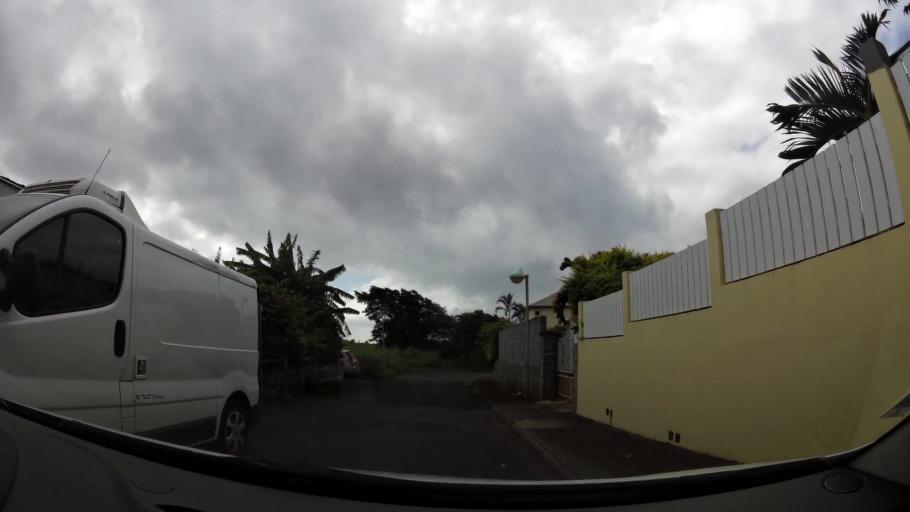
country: RE
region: Reunion
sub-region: Reunion
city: Sainte-Marie
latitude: -20.8960
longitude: 55.5628
